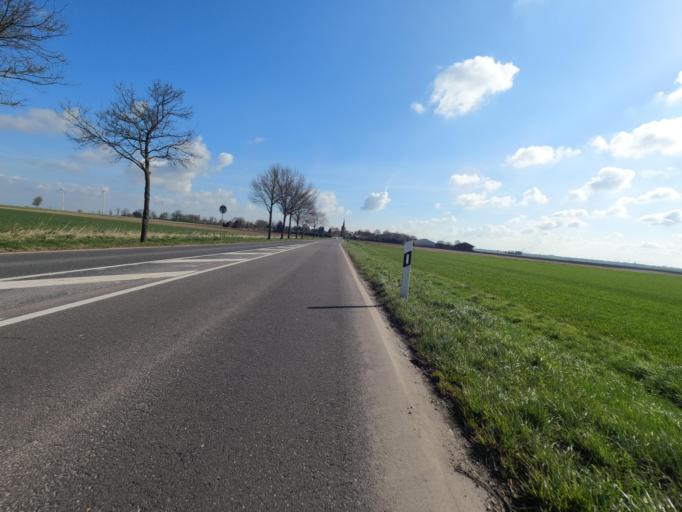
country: DE
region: North Rhine-Westphalia
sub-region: Regierungsbezirk Koln
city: Linnich
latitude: 50.9957
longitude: 6.3379
